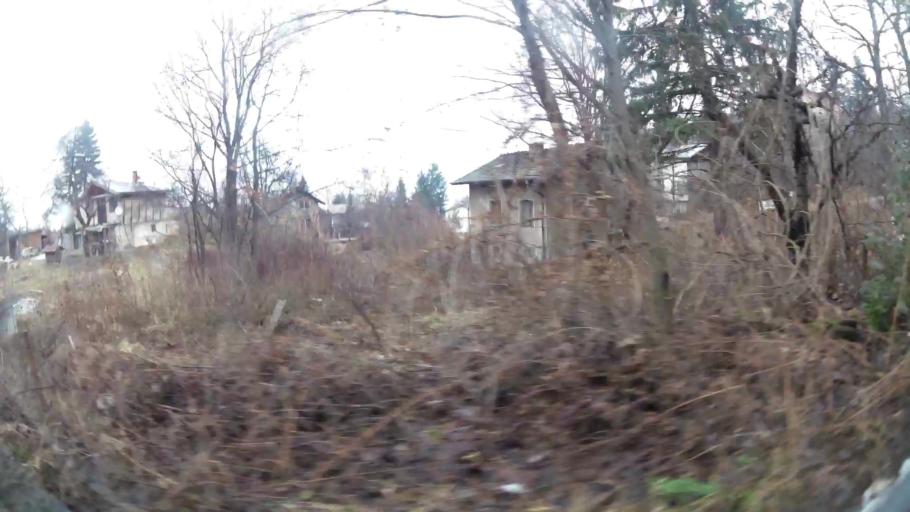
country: BG
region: Sofia-Capital
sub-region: Stolichna Obshtina
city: Sofia
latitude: 42.6011
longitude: 23.3874
